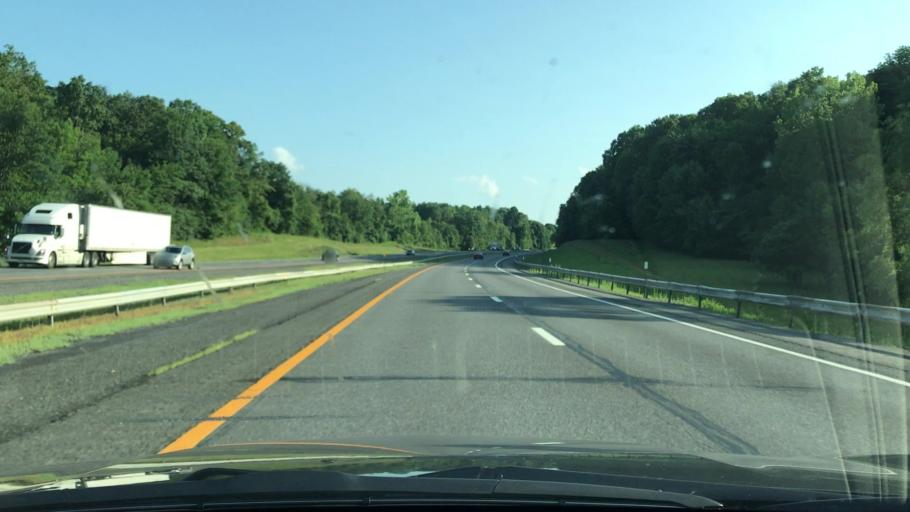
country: US
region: New York
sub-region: Greene County
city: Coxsackie
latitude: 42.3720
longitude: -73.8433
